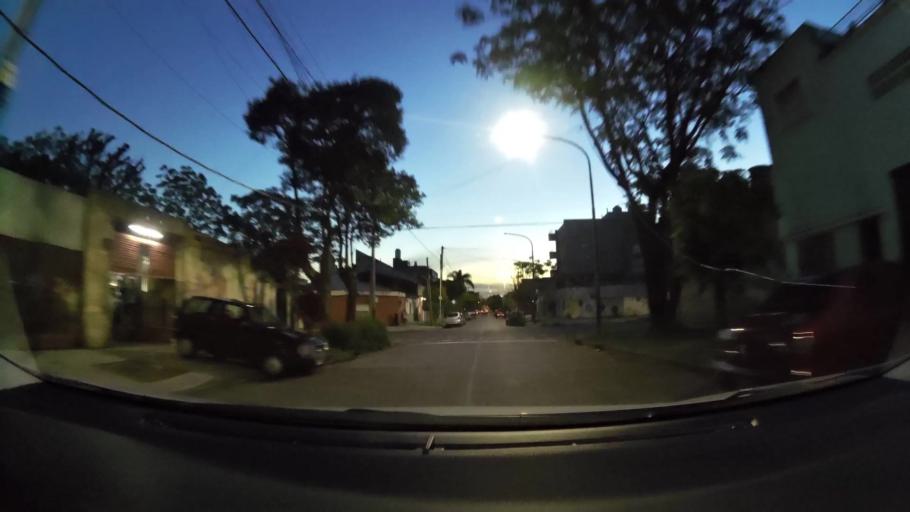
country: AR
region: Buenos Aires F.D.
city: Villa Lugano
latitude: -34.6854
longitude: -58.4795
